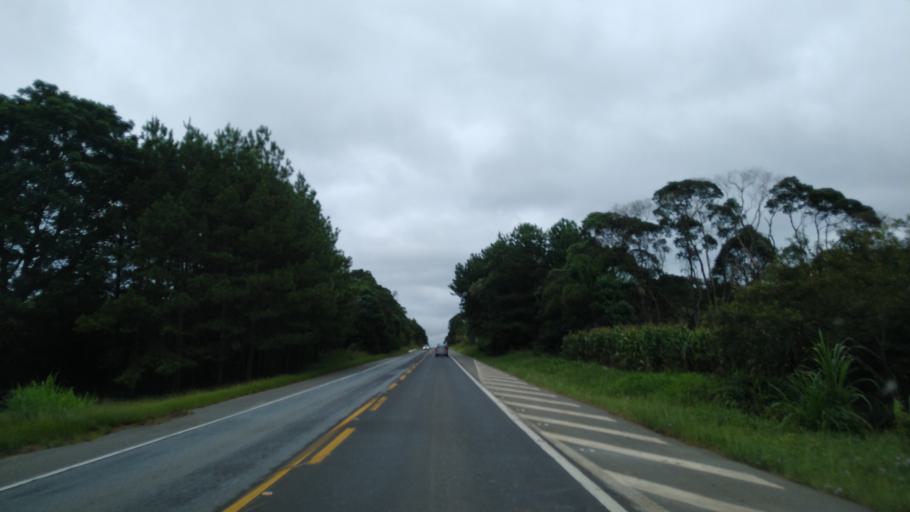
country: BR
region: Santa Catarina
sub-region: Tres Barras
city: Tres Barras
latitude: -26.1700
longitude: -50.1513
